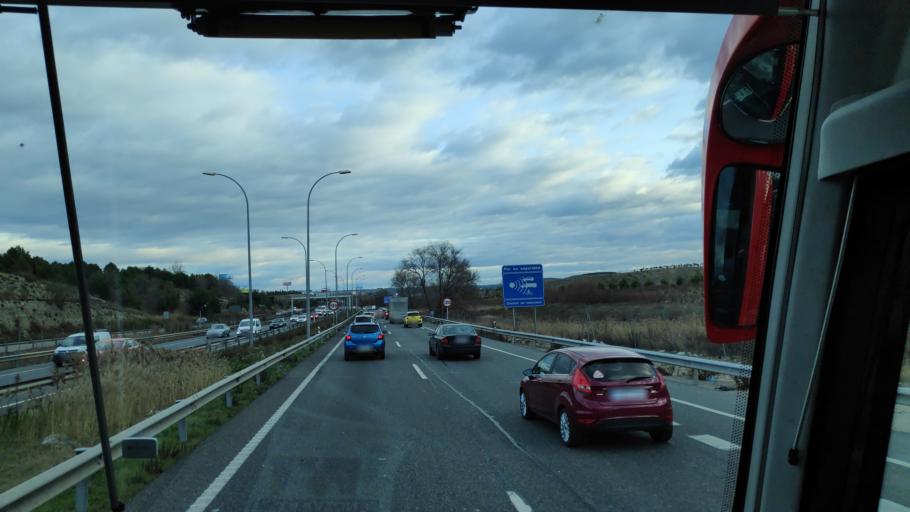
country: ES
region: Madrid
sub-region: Provincia de Madrid
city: Vaciamadrid
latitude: 40.3499
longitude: -3.5481
